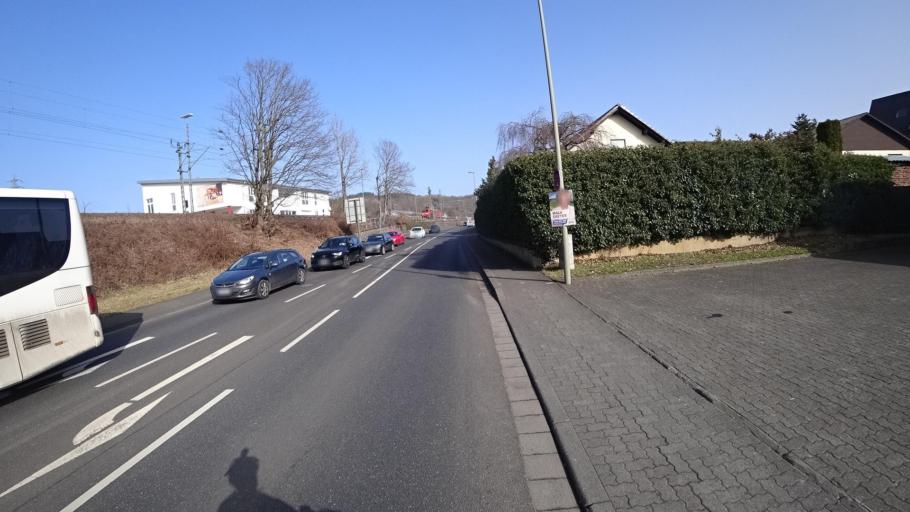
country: DE
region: Rheinland-Pfalz
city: Wissen
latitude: 50.7816
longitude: 7.7285
